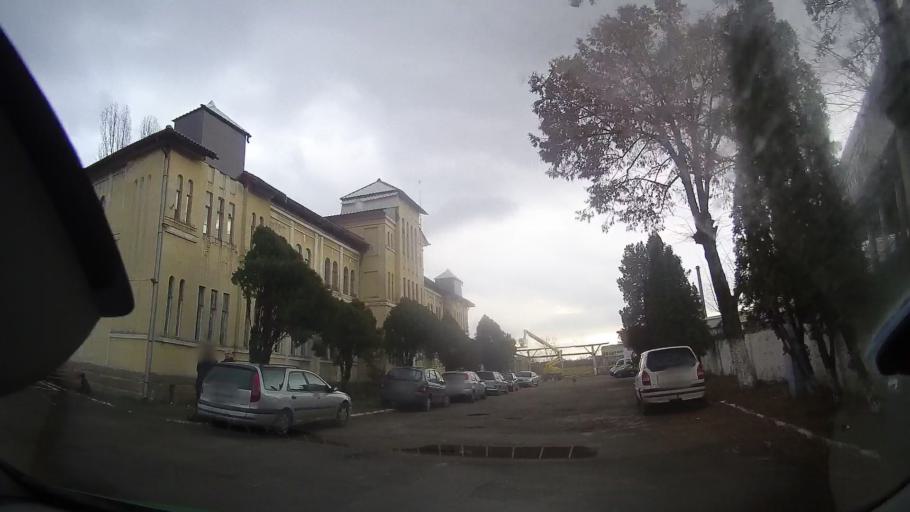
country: RO
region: Cluj
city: Turda
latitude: 46.5562
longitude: 23.7922
